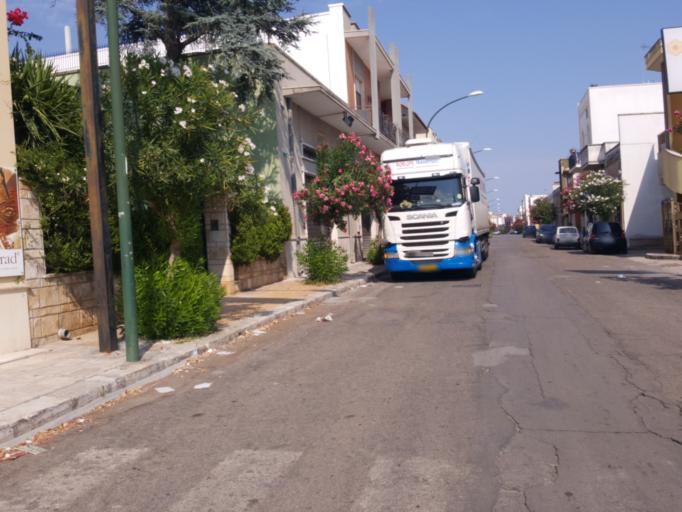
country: IT
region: Apulia
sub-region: Provincia di Lecce
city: Campi Salentina
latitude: 40.3988
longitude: 18.0116
